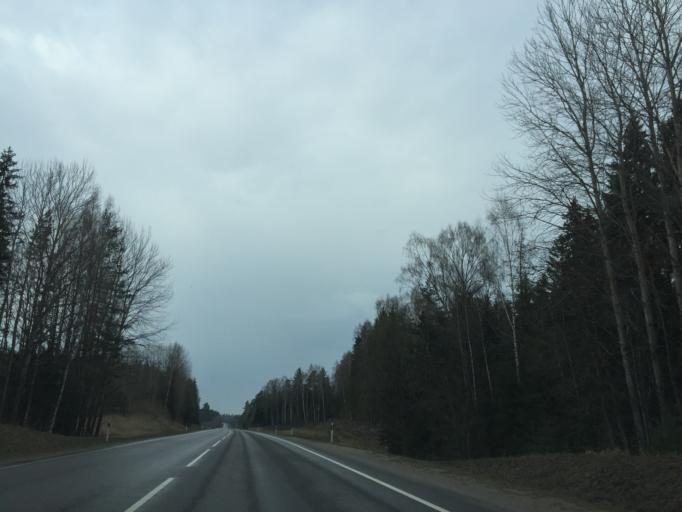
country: EE
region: Tartu
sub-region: UElenurme vald
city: Ulenurme
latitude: 58.1047
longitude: 26.7398
